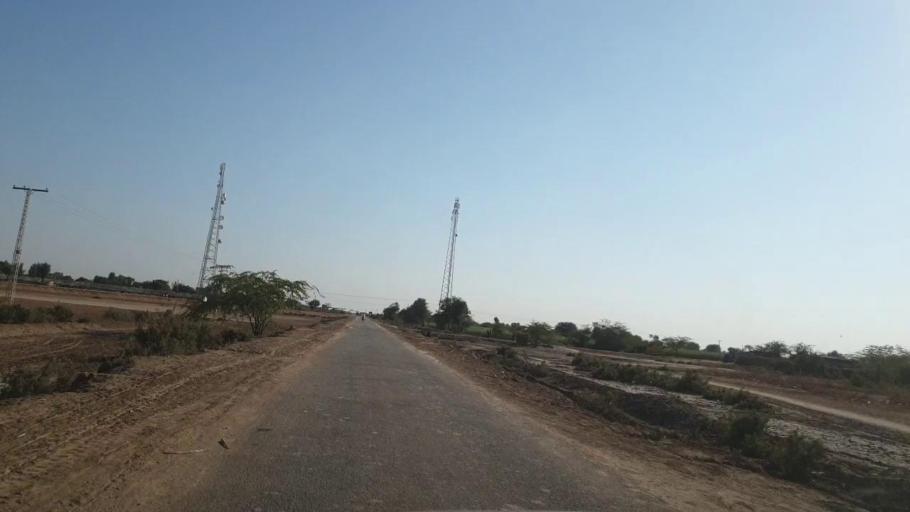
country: PK
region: Sindh
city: Mirpur Khas
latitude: 25.6189
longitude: 69.0826
